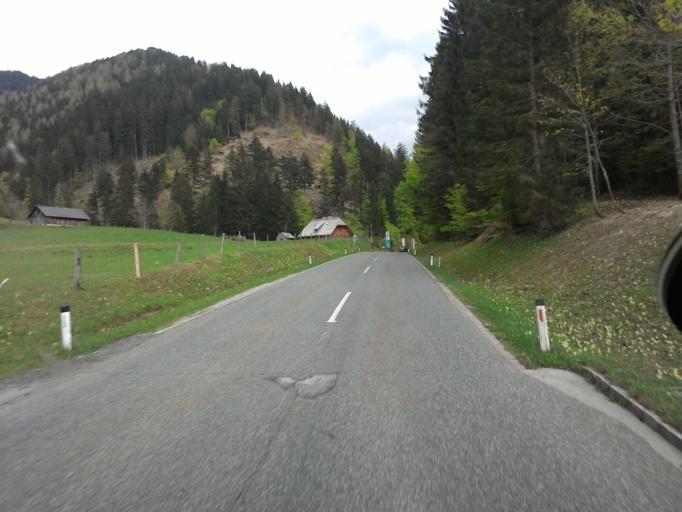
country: AT
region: Styria
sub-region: Politischer Bezirk Liezen
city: Hall
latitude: 47.7032
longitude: 14.4591
